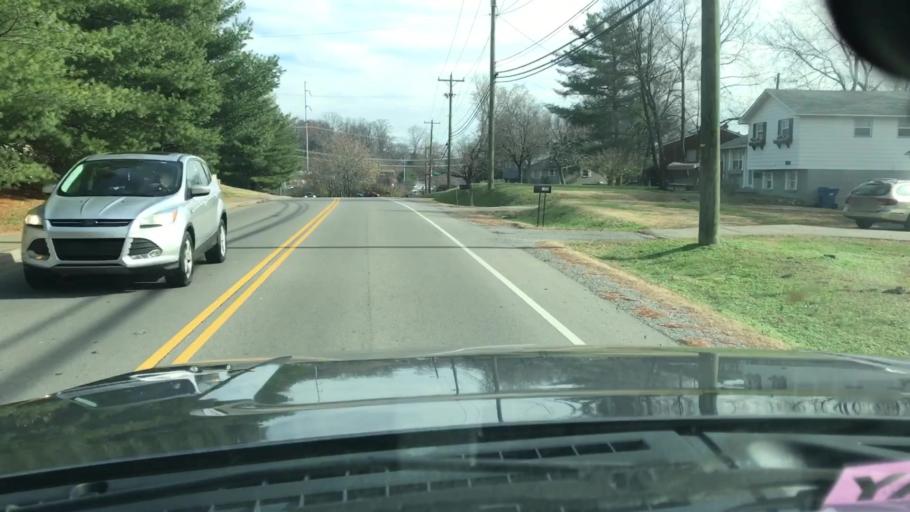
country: US
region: Tennessee
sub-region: Davidson County
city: Lakewood
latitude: 36.1923
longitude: -86.6188
